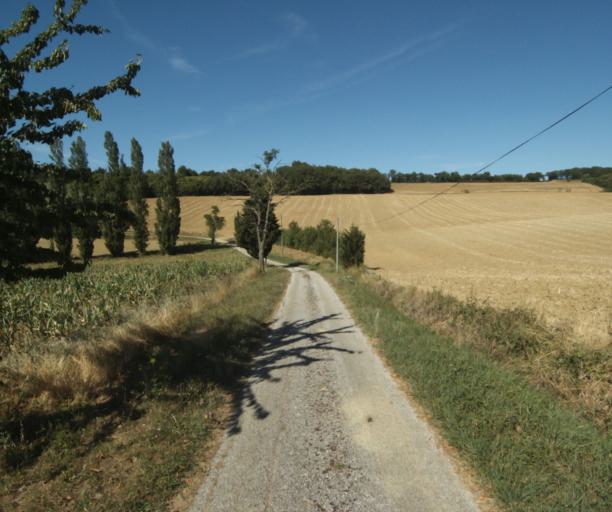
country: FR
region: Midi-Pyrenees
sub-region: Departement de la Haute-Garonne
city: Saint-Felix-Lauragais
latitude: 43.5187
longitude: 1.9079
